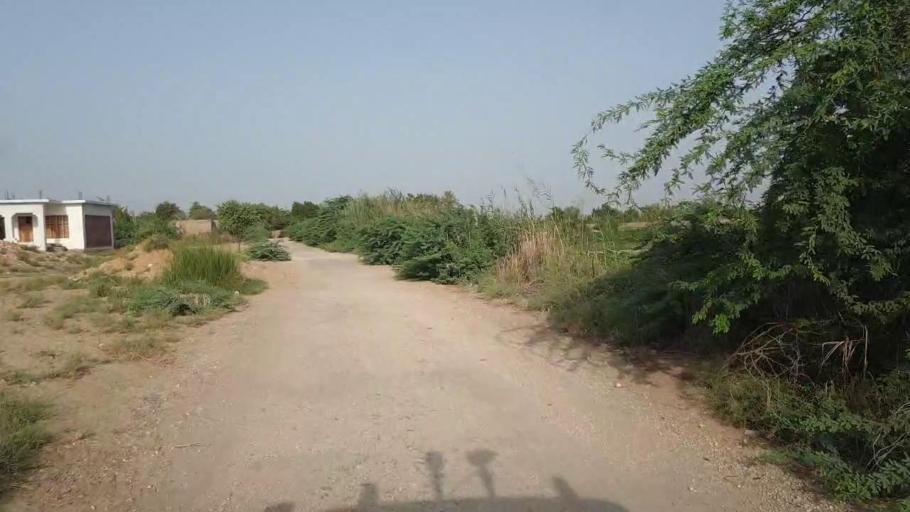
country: PK
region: Sindh
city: Daur
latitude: 26.3418
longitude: 68.2840
